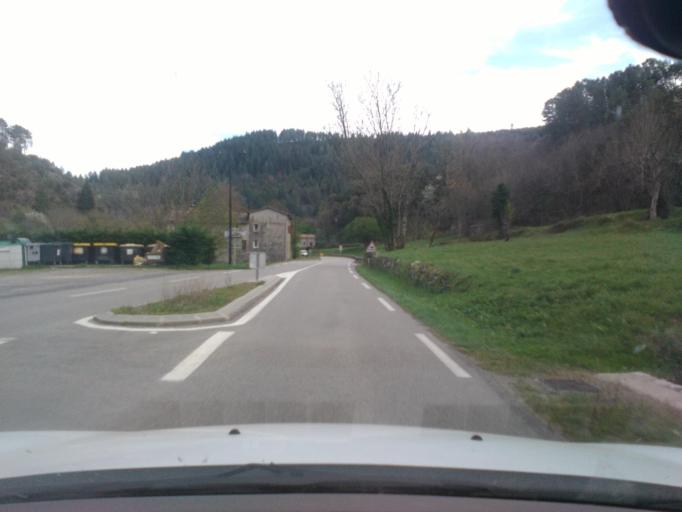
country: FR
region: Languedoc-Roussillon
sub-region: Departement du Gard
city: Lasalle
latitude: 44.1159
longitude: 3.7654
